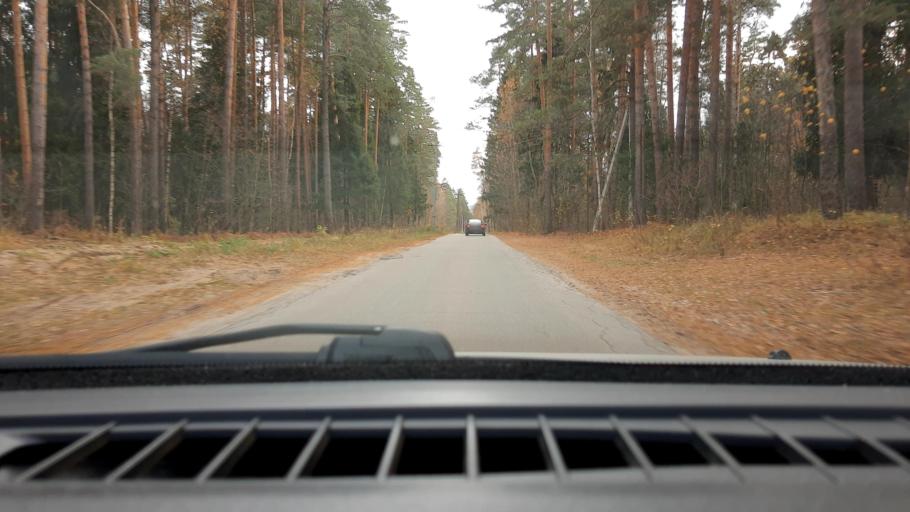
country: RU
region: Nizjnij Novgorod
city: Afonino
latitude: 56.1731
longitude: 44.0977
